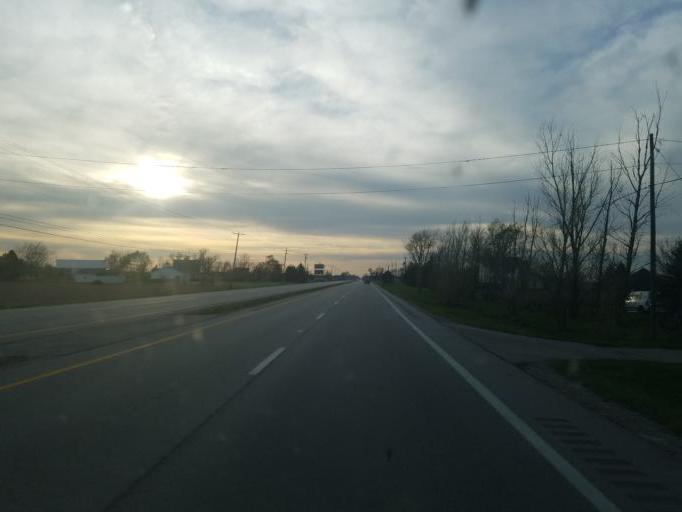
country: US
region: Ohio
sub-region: Sandusky County
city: Gibsonburg
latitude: 41.4150
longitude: -83.2752
